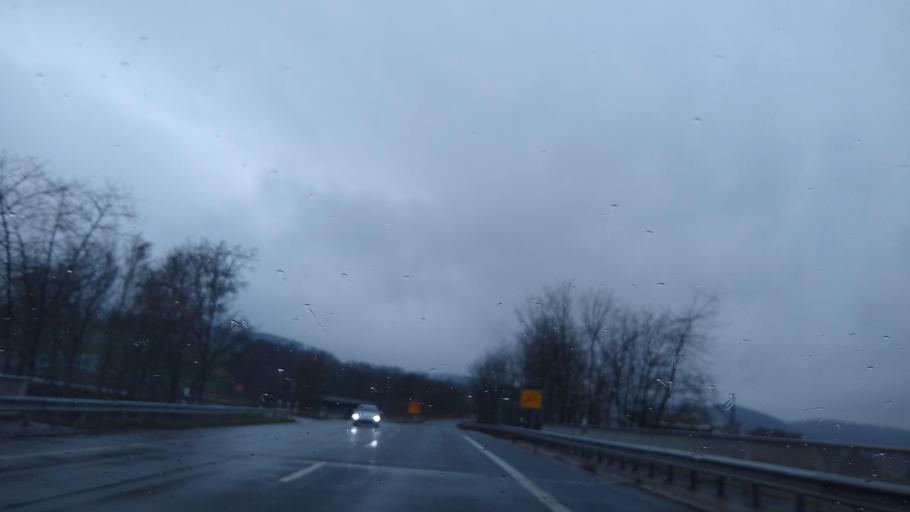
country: DE
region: Lower Saxony
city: Hehlen
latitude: 51.9855
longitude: 9.4928
